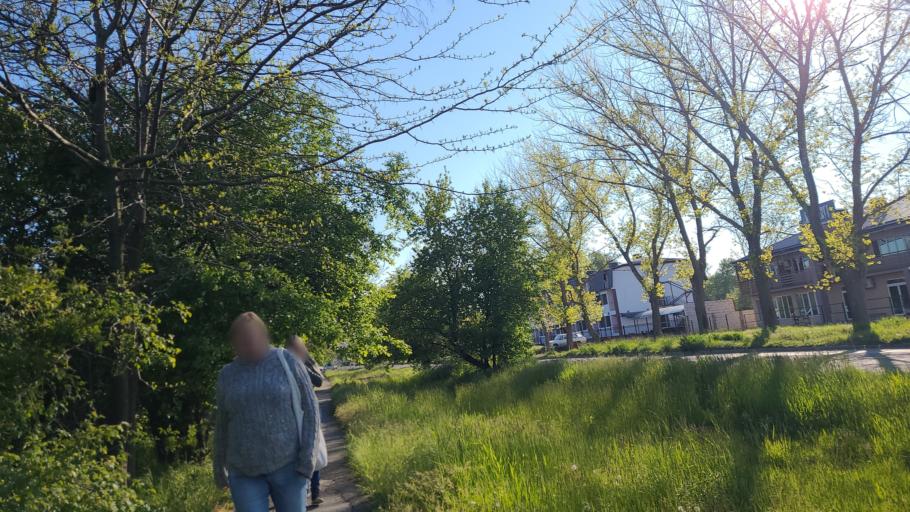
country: RU
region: Krasnodarskiy
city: Tsibanobalka
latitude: 44.9476
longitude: 37.3078
